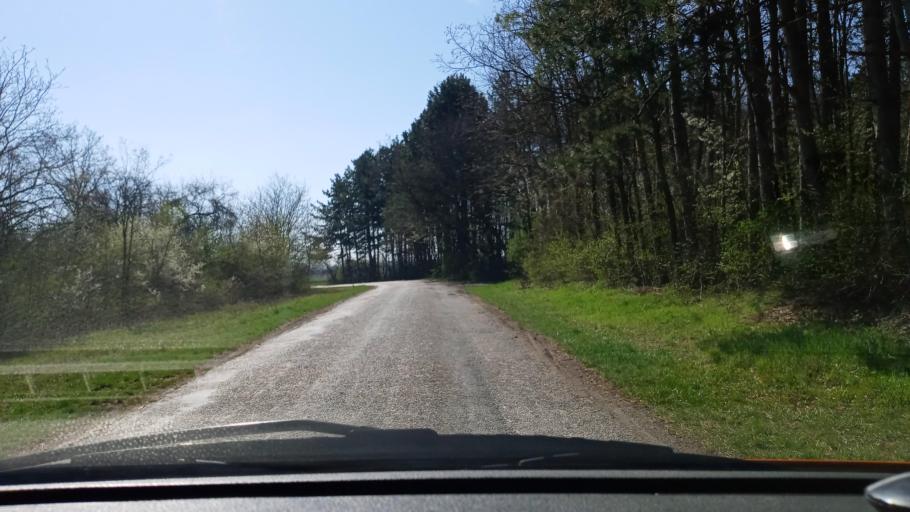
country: HU
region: Baranya
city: Kozarmisleny
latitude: 46.0770
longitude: 18.3511
